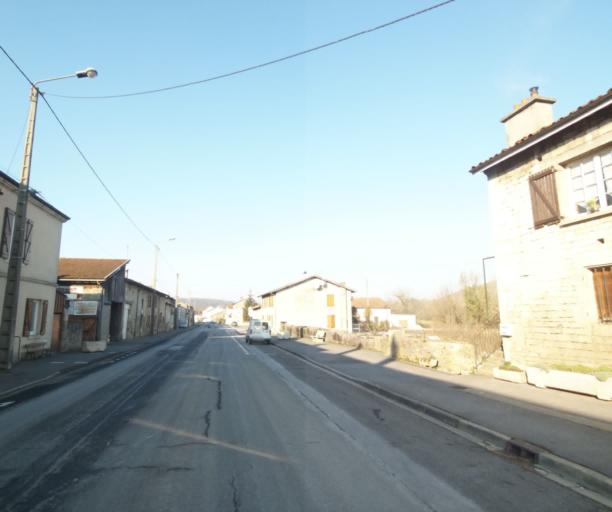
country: FR
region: Champagne-Ardenne
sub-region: Departement de la Haute-Marne
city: Chevillon
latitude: 48.5228
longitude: 5.1042
